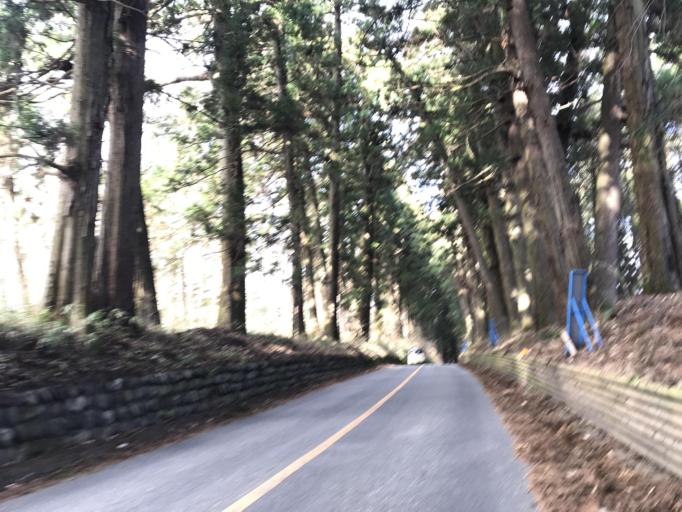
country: JP
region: Tochigi
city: Imaichi
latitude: 36.6874
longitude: 139.7180
